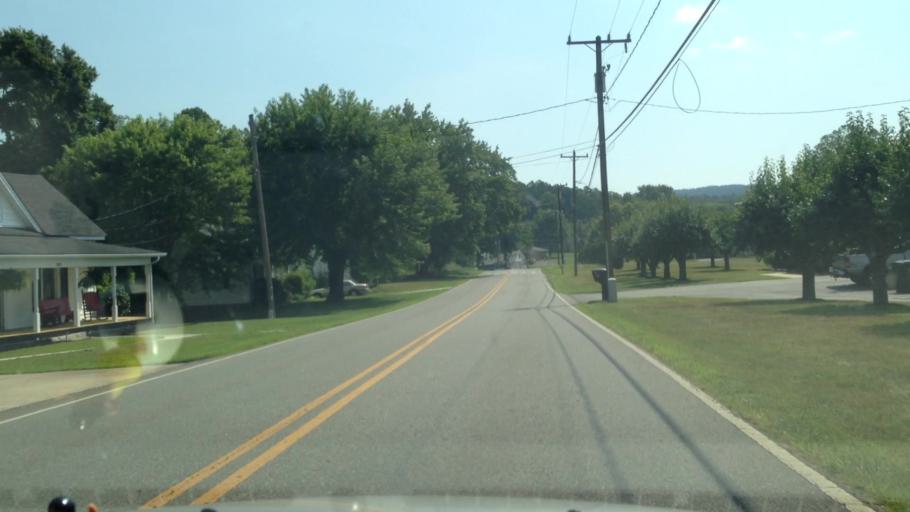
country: US
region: North Carolina
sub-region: Surry County
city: Flat Rock
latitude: 36.5131
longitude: -80.5669
